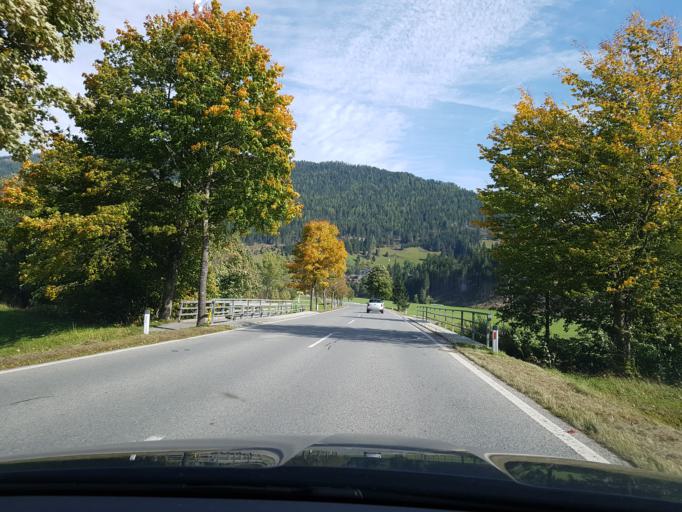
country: AT
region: Carinthia
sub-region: Politischer Bezirk Spittal an der Drau
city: Kleinkirchheim
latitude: 46.8487
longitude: 13.8873
